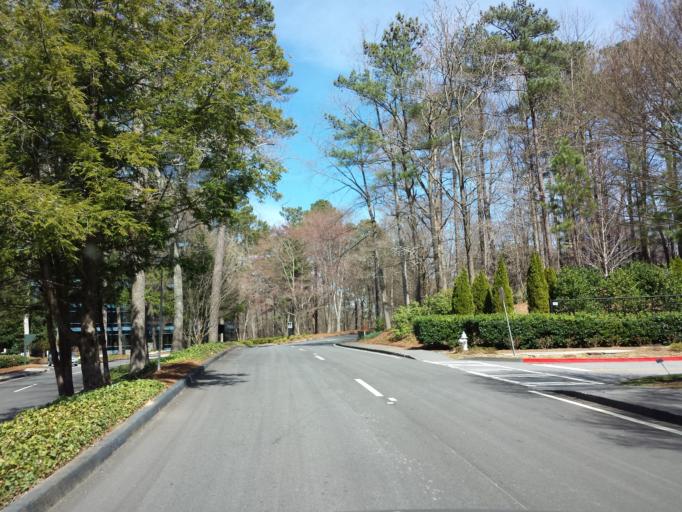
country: US
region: Georgia
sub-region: Cobb County
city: Vinings
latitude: 33.9038
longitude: -84.4571
